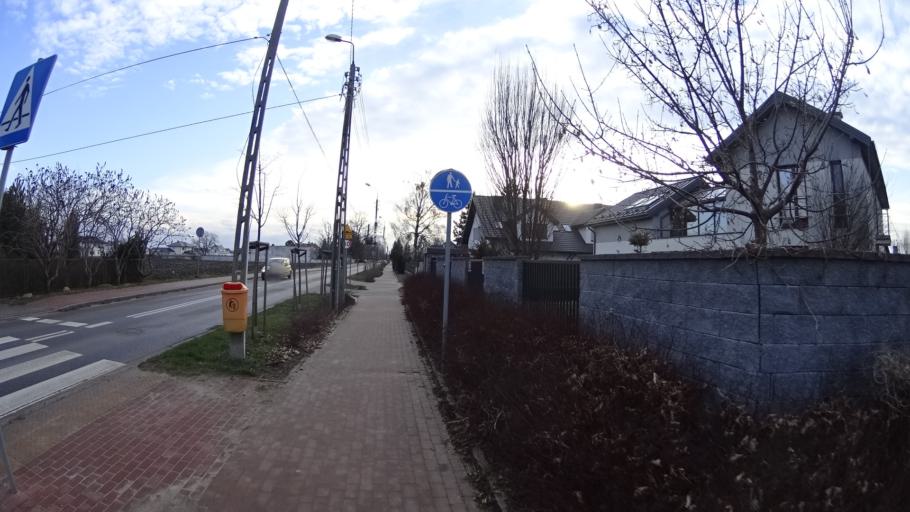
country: PL
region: Masovian Voivodeship
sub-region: Powiat warszawski zachodni
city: Ozarow Mazowiecki
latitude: 52.2268
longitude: 20.8020
